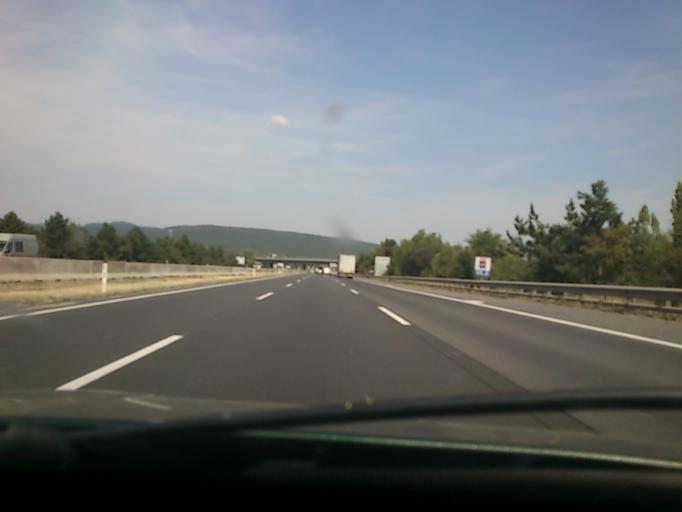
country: AT
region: Lower Austria
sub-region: Politischer Bezirk Wiener Neustadt
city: Weikersdorf am Steinfelde
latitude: 47.8153
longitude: 16.1932
